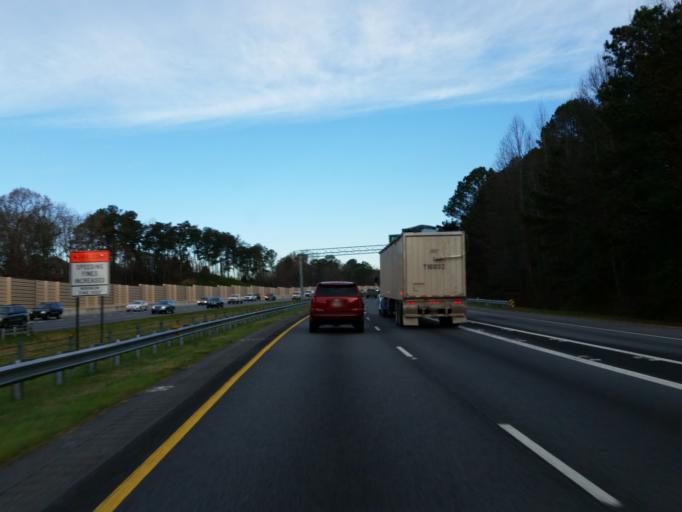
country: US
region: Georgia
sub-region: Cherokee County
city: Woodstock
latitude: 34.1075
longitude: -84.5331
